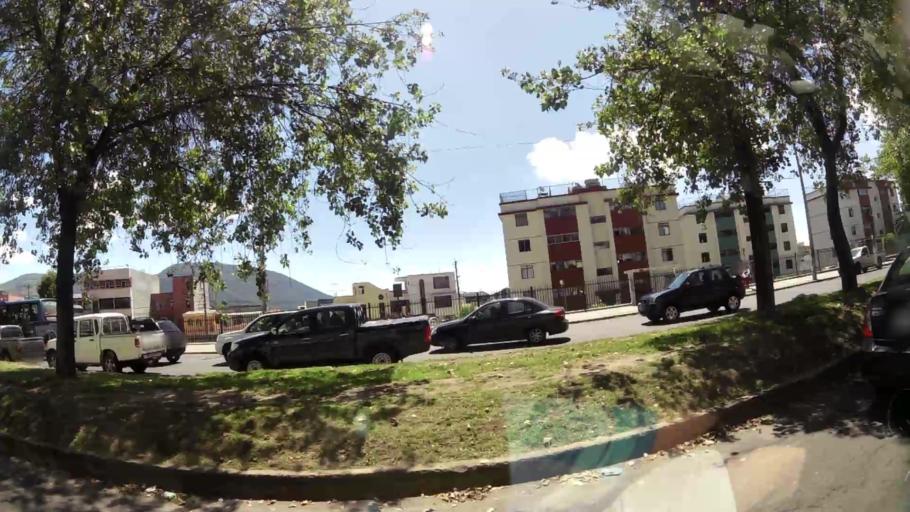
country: EC
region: Pichincha
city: Quito
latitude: -0.0910
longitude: -78.4740
